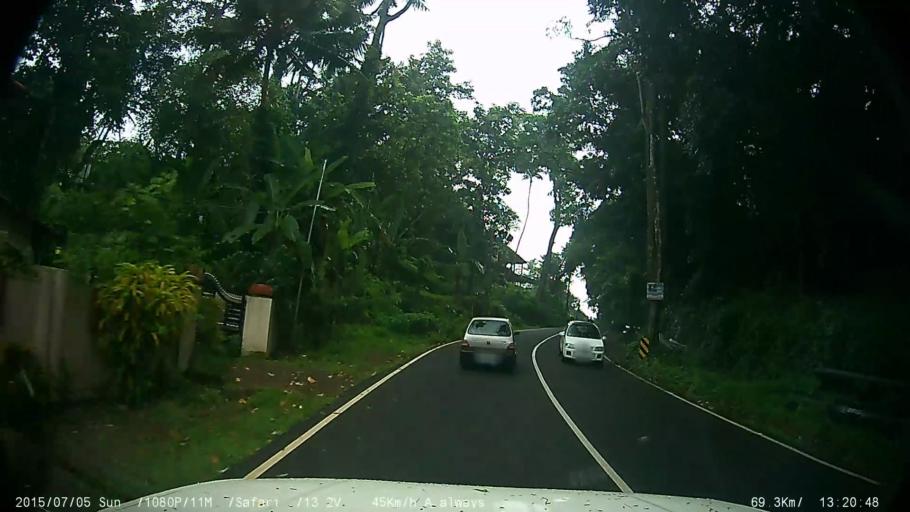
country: IN
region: Kerala
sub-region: Kottayam
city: Kottayam
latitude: 9.5821
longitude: 76.5821
